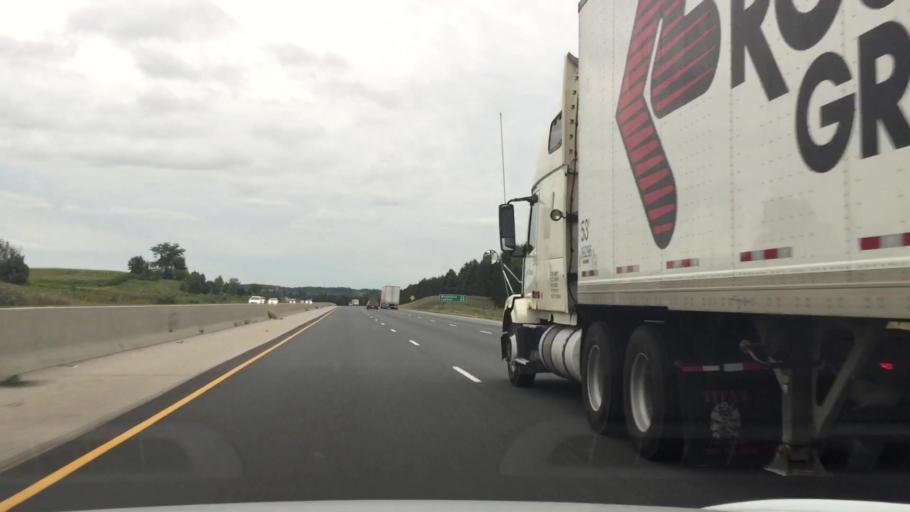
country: CA
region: Ontario
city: Kitchener
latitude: 43.3224
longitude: -80.4615
